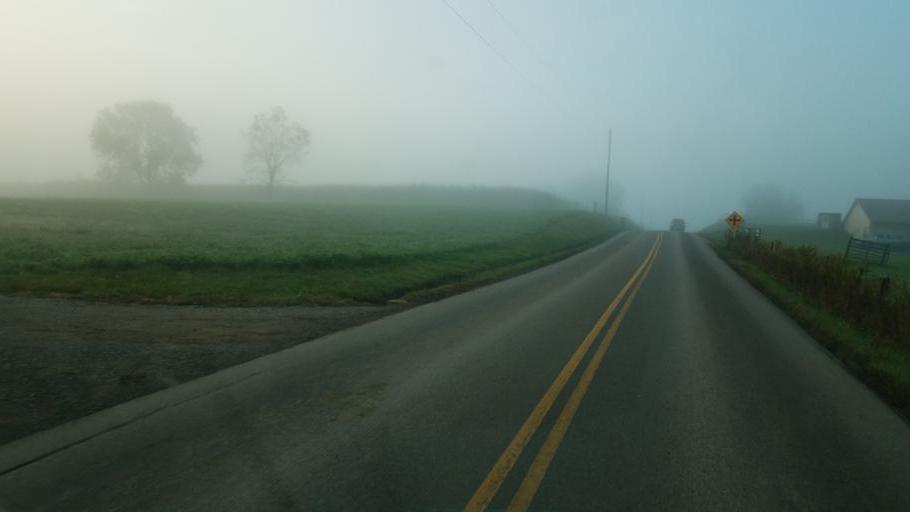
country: US
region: Ohio
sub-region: Holmes County
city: Millersburg
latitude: 40.5659
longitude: -81.7817
